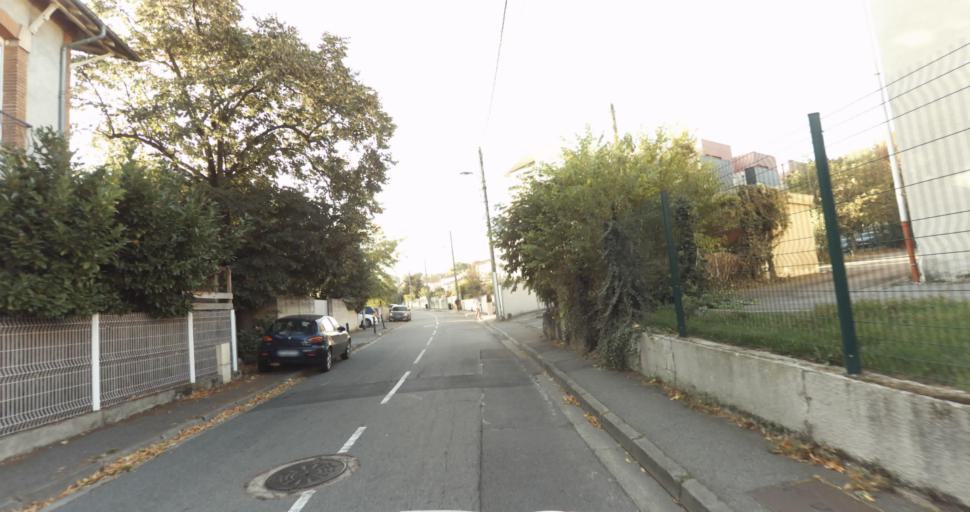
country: FR
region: Midi-Pyrenees
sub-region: Departement de la Haute-Garonne
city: Ramonville-Saint-Agne
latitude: 43.5546
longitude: 1.4668
